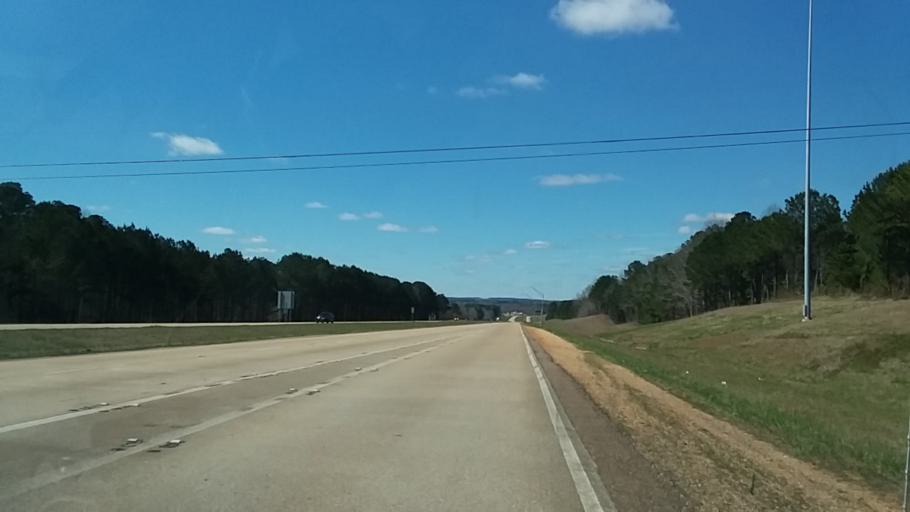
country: US
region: Mississippi
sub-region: Tishomingo County
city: Iuka
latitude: 34.7950
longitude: -88.2132
